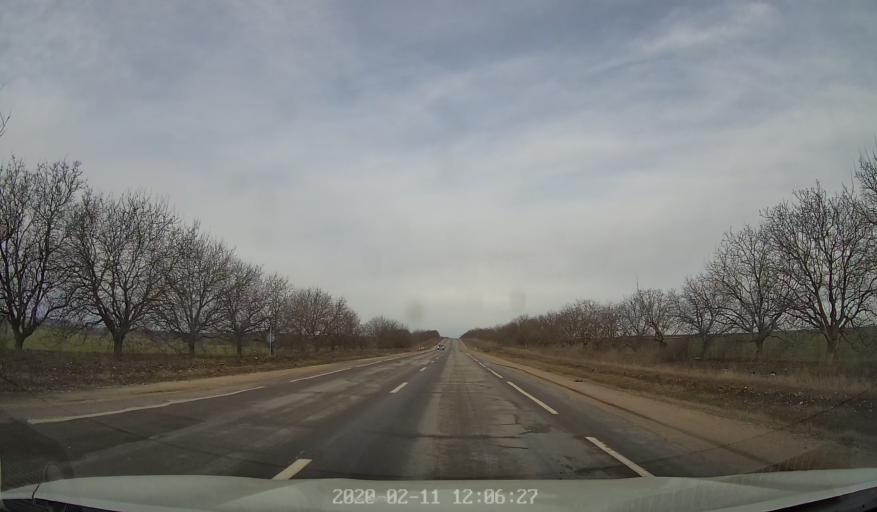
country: MD
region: Riscani
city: Riscani
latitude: 47.9952
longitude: 27.5725
